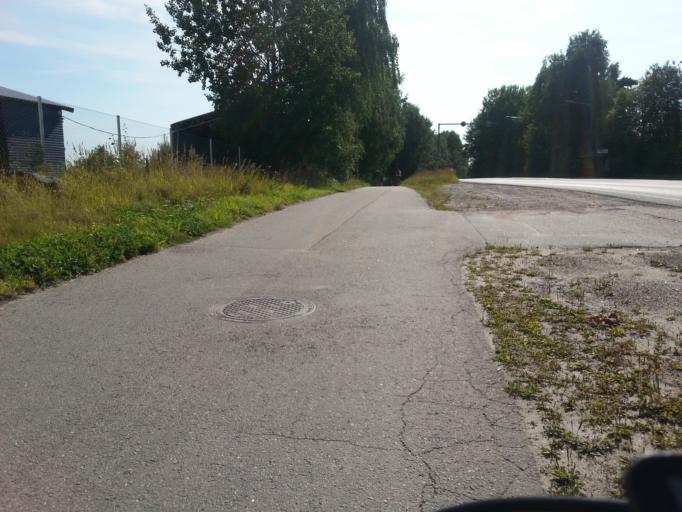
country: FI
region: Uusimaa
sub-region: Helsinki
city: Helsinki
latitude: 60.2243
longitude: 24.9959
